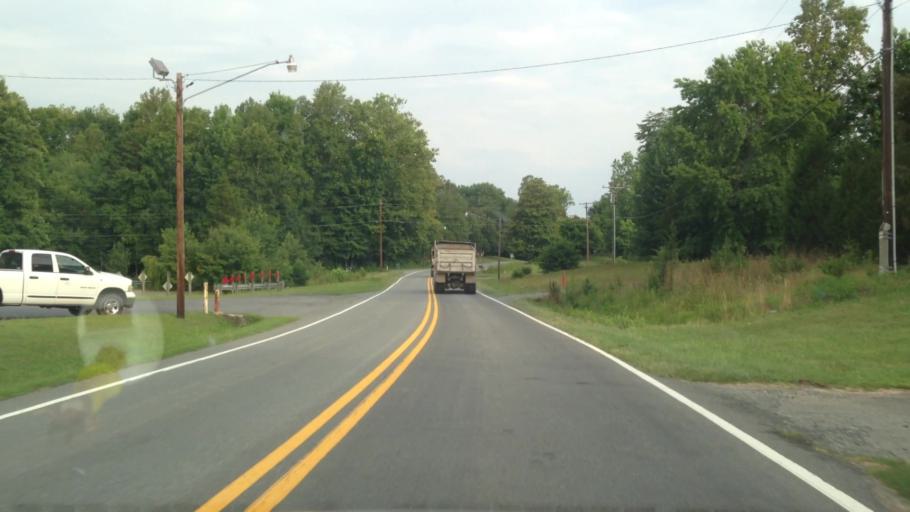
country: US
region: North Carolina
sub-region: Forsyth County
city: Walkertown
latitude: 36.1747
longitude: -80.1714
